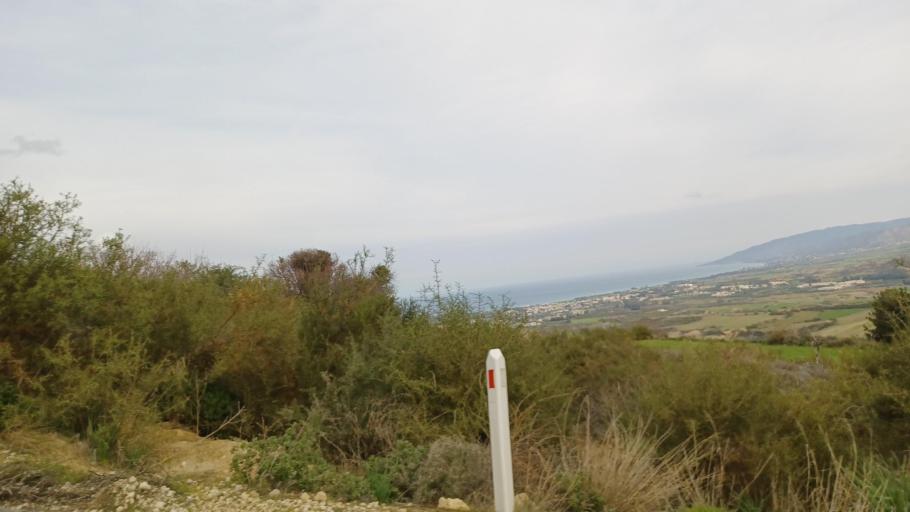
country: CY
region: Pafos
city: Polis
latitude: 35.0025
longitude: 32.4088
